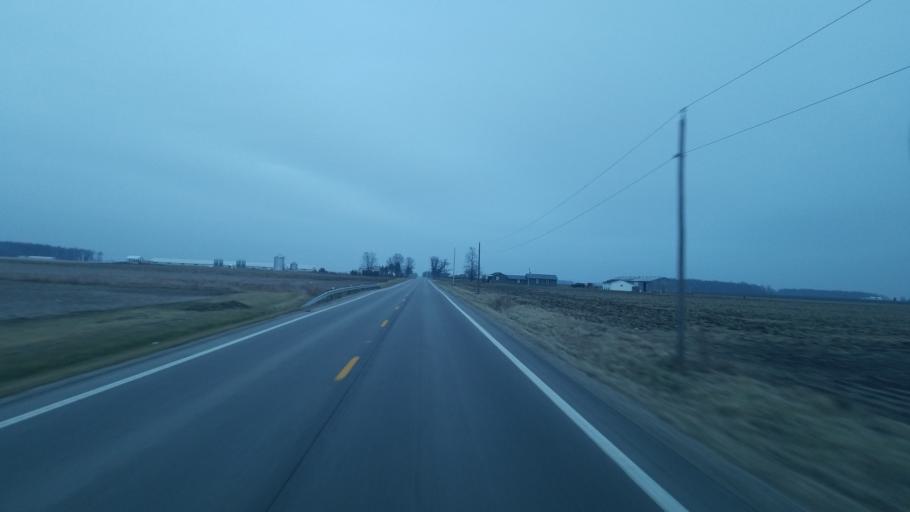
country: US
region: Ohio
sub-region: Mercer County
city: Rockford
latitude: 40.6549
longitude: -84.6832
